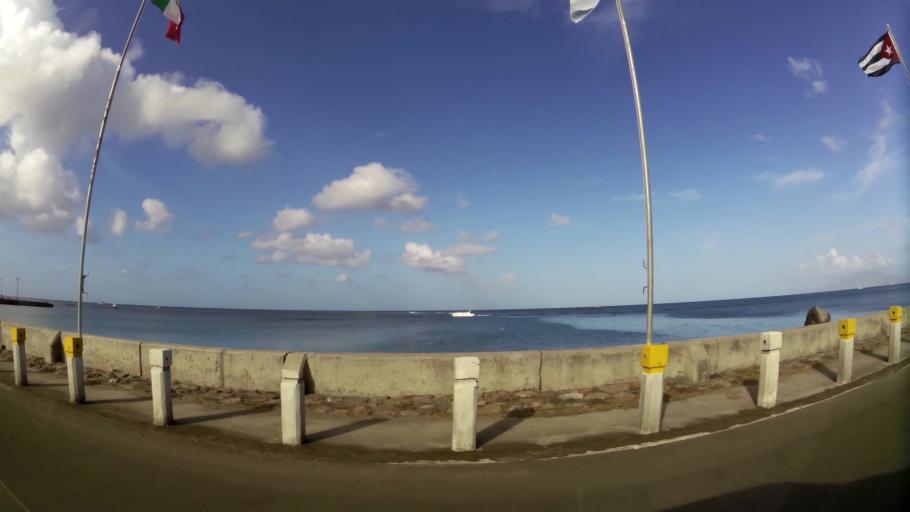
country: KN
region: Saint Paul Charlestown
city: Charlestown
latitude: 17.1404
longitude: -62.6298
